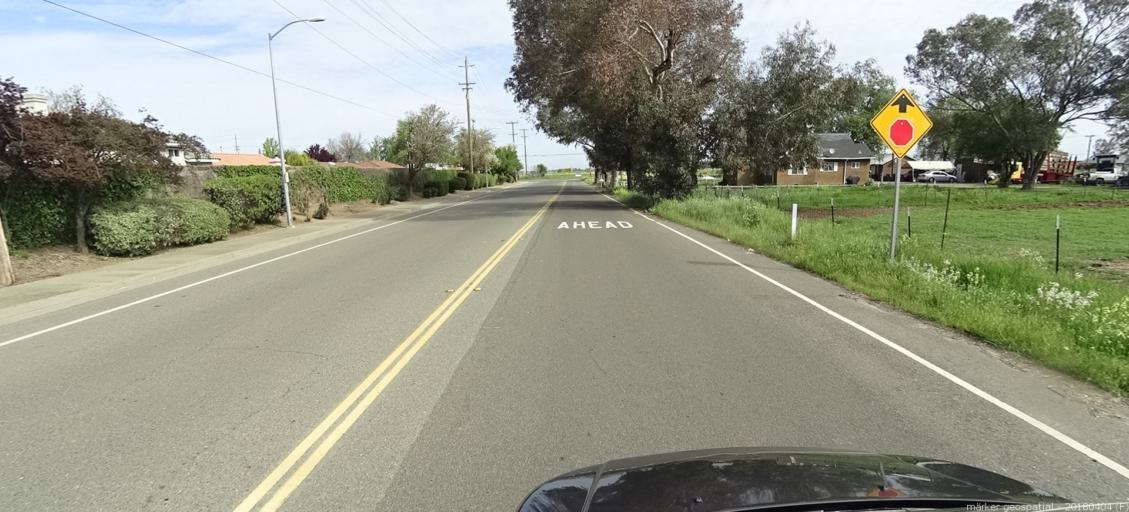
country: US
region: California
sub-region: Sacramento County
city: Herald
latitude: 38.2899
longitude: -121.2828
